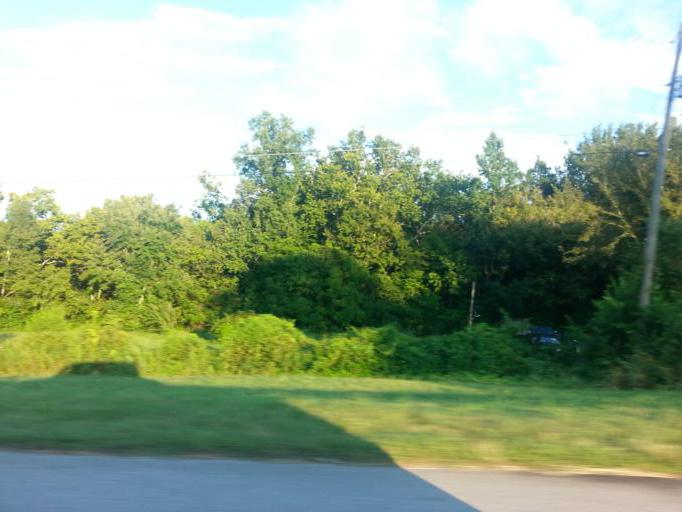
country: US
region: Tennessee
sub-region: Knox County
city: Mascot
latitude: 36.0774
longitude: -83.7686
